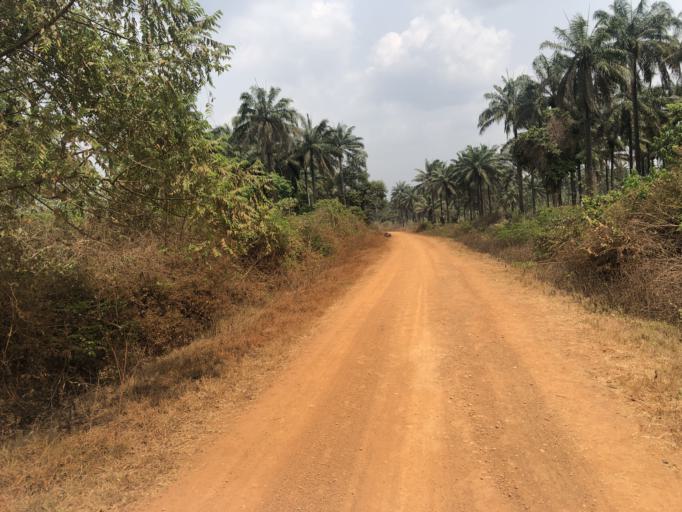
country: NG
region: Osun
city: Bode Osi
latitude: 7.7561
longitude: 4.2554
